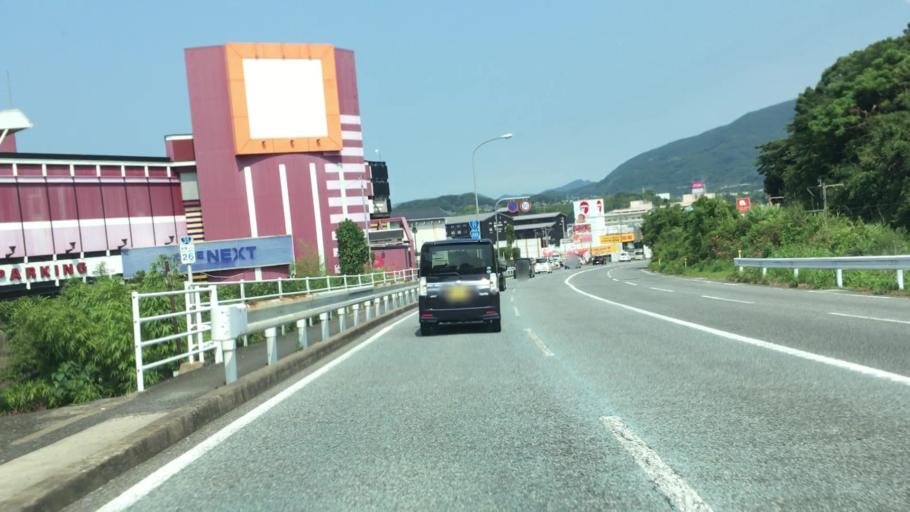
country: JP
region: Nagasaki
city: Sasebo
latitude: 33.1425
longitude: 129.7881
